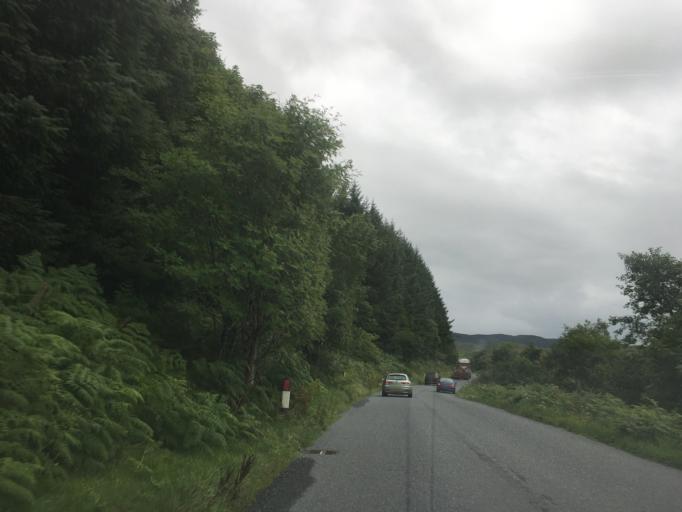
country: GB
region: Scotland
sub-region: Argyll and Bute
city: Oban
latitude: 56.2736
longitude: -5.4778
